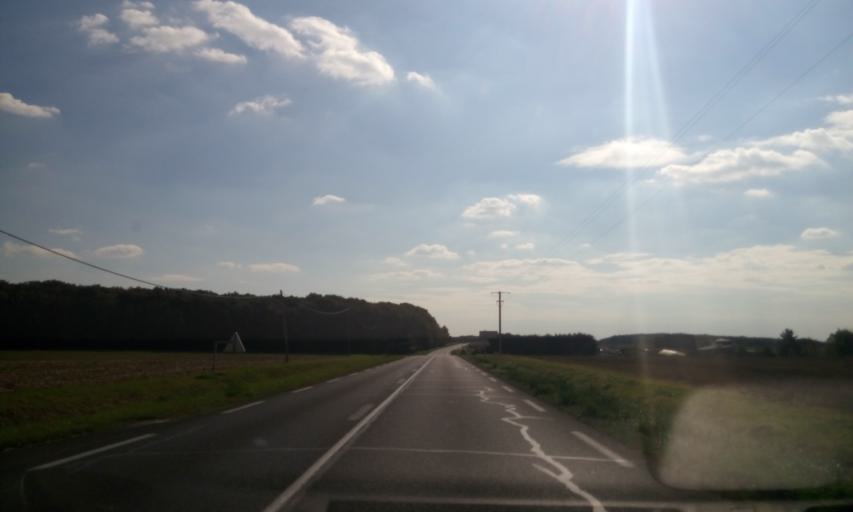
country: FR
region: Centre
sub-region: Departement d'Indre-et-Loire
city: Poce-sur-Cisse
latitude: 47.4818
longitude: 1.0082
